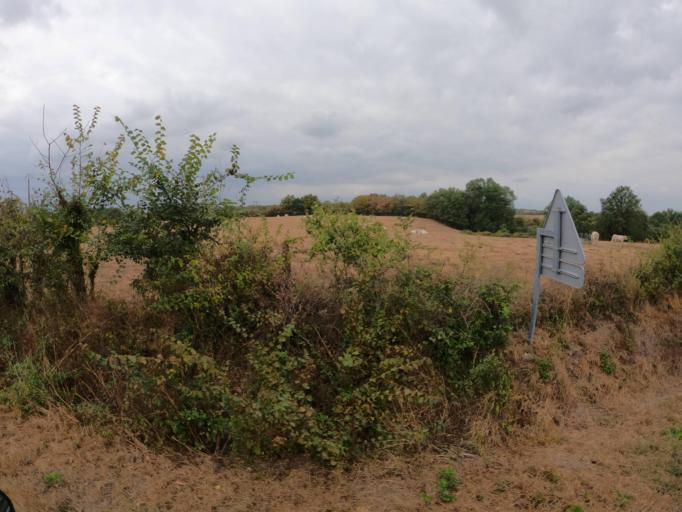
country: FR
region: Pays de la Loire
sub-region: Departement de la Vendee
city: Tiffauges
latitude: 46.9980
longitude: -1.1083
